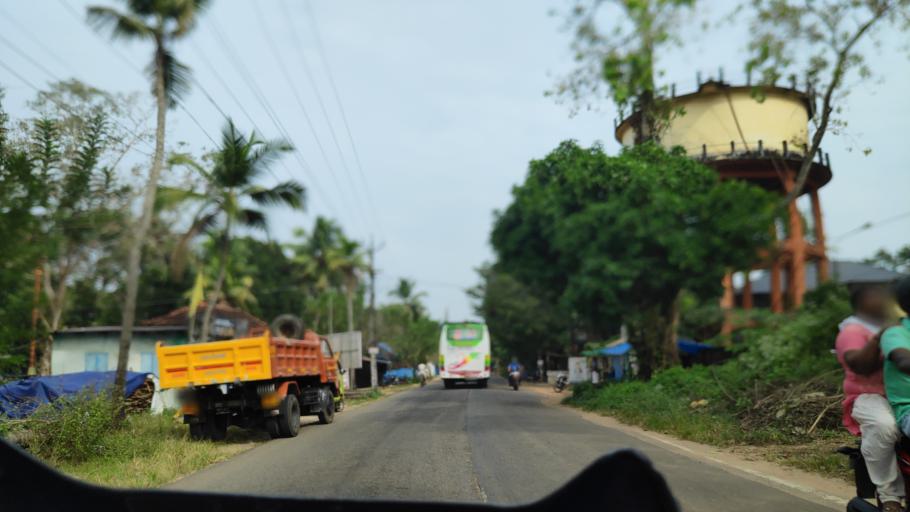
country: IN
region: Kerala
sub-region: Alappuzha
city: Kutiatodu
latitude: 9.8134
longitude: 76.3519
